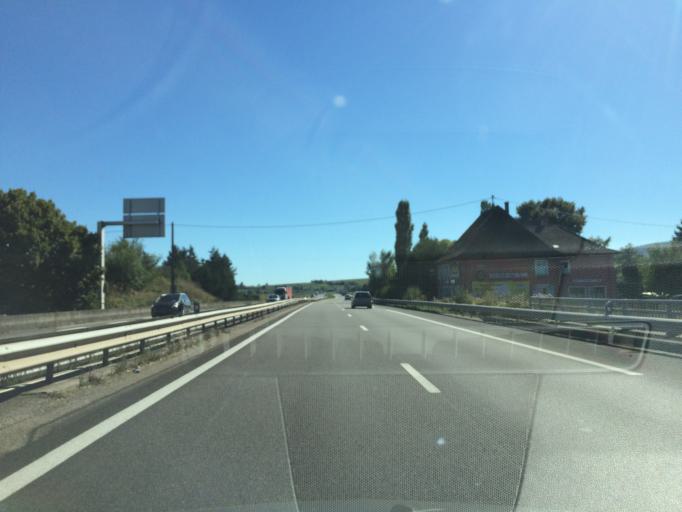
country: FR
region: Alsace
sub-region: Departement du Haut-Rhin
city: Eguisheim
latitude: 48.0408
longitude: 7.3221
